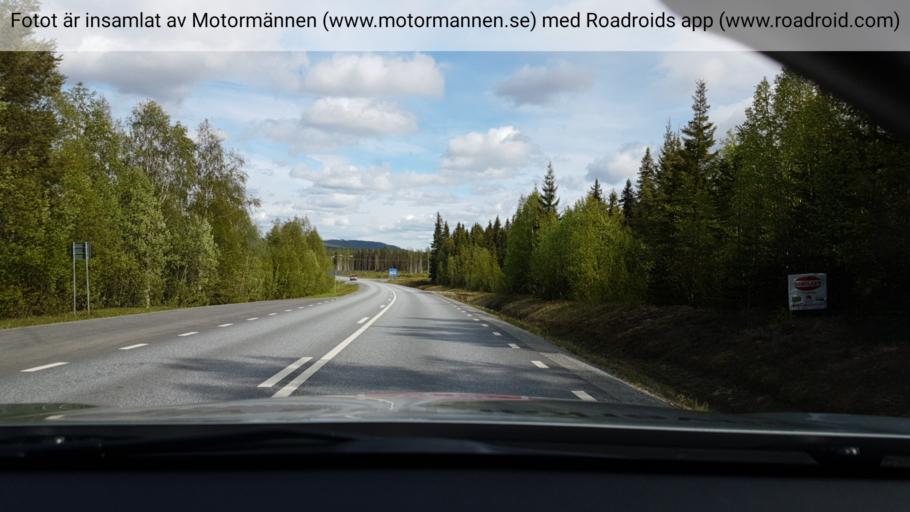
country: SE
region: Vaesterbotten
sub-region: Lycksele Kommun
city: Lycksele
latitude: 64.0699
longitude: 18.3915
